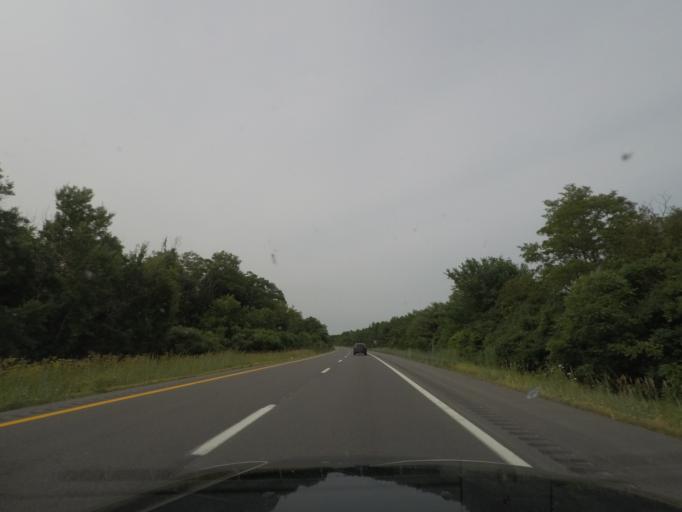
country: US
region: New York
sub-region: Clinton County
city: Cumberland Head
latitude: 44.7461
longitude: -73.4274
